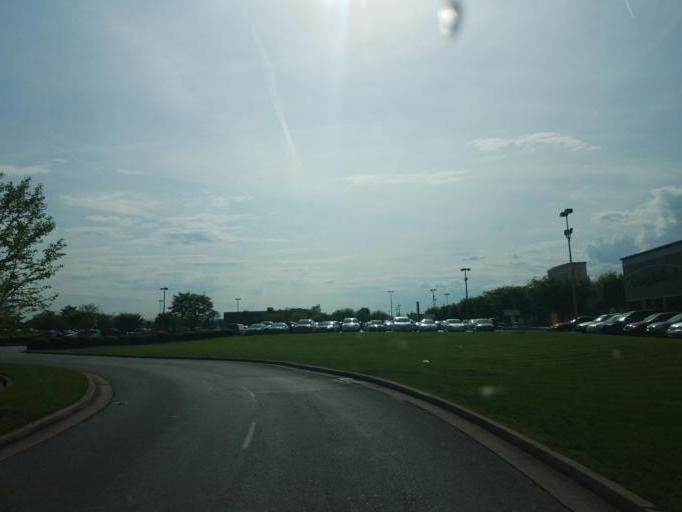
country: US
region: Kentucky
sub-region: Warren County
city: Bowling Green
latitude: 36.9521
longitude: -86.4277
